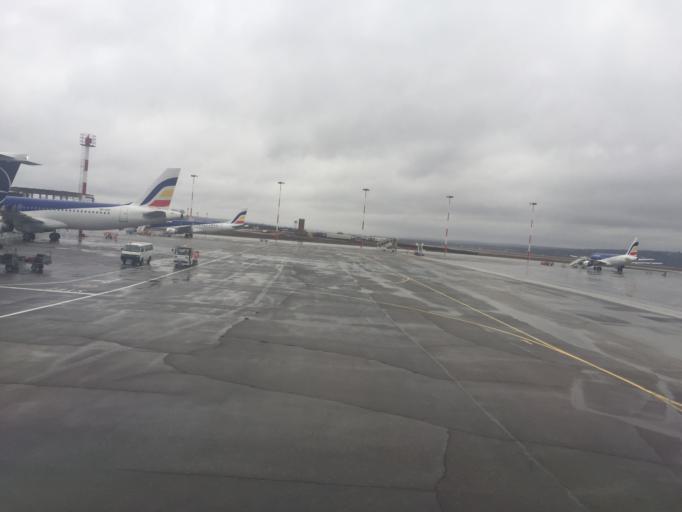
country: MD
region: Chisinau
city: Singera
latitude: 46.9334
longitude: 28.9348
